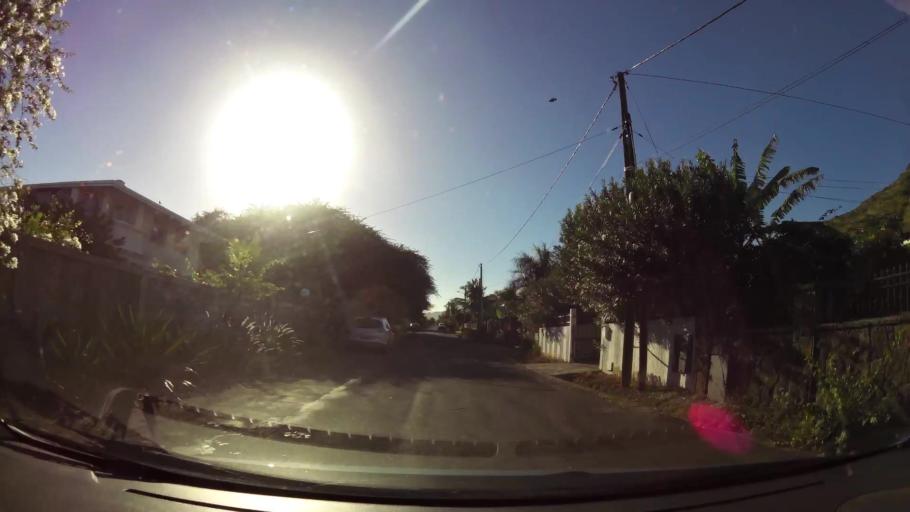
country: MU
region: Black River
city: Tamarin
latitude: -20.3373
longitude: 57.3706
